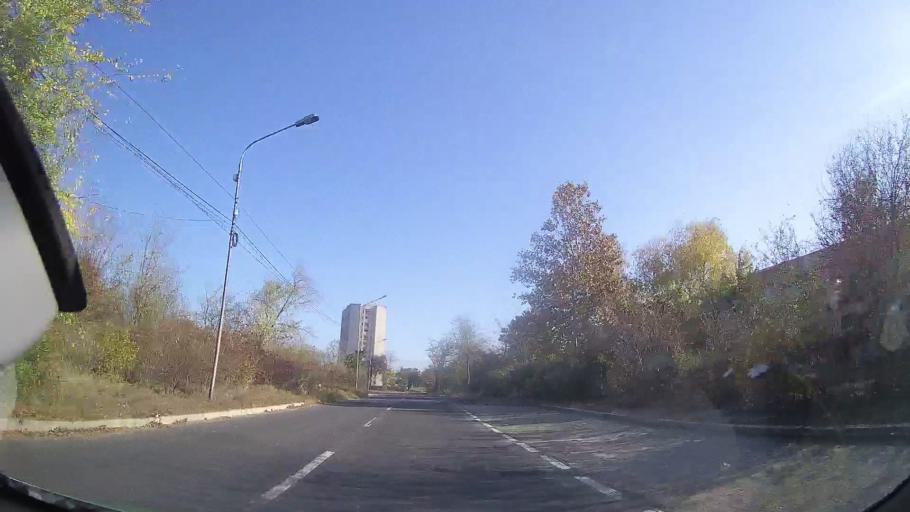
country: RO
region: Constanta
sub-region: Municipiul Mangalia
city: Mangalia
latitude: 43.8479
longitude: 28.5938
